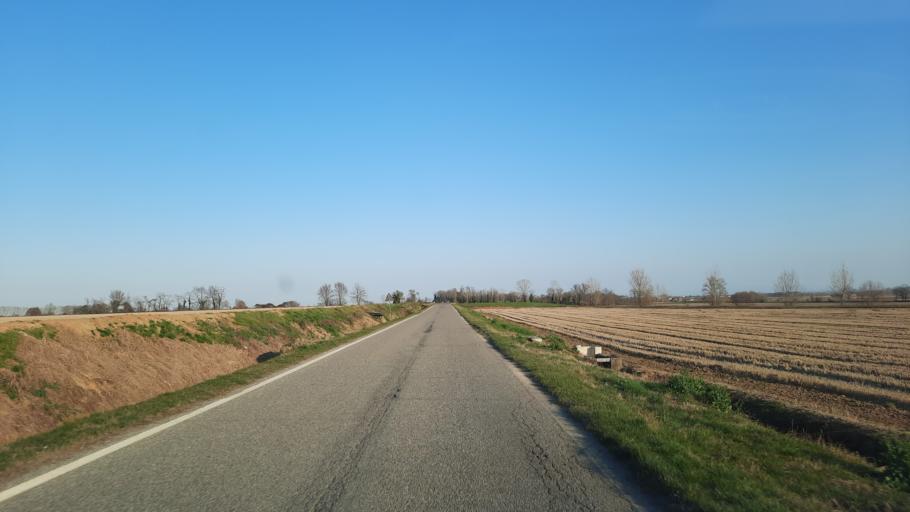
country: IT
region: Piedmont
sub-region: Provincia di Vercelli
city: Tricerro
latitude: 45.2059
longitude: 8.3479
